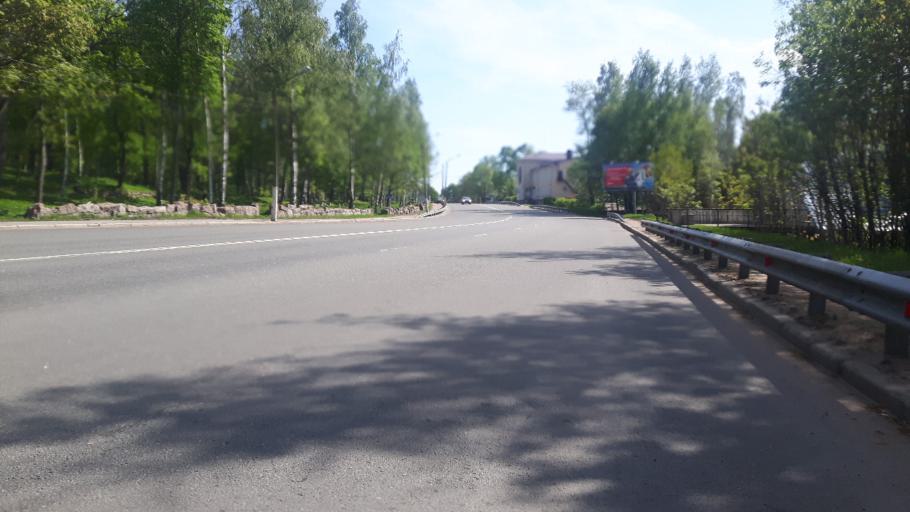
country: RU
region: Leningrad
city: Vyborg
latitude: 60.7331
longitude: 28.6981
